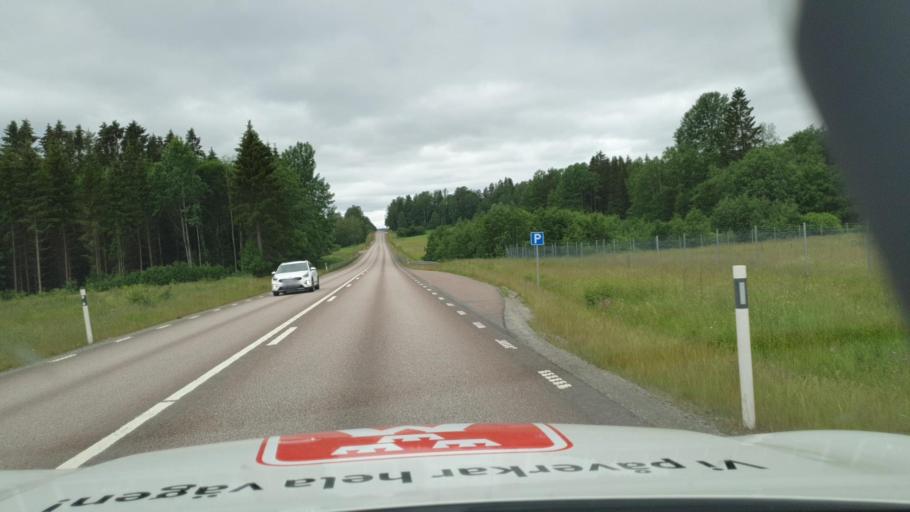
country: SE
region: Vaermland
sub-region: Arvika Kommun
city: Arvika
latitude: 59.6665
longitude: 12.8545
